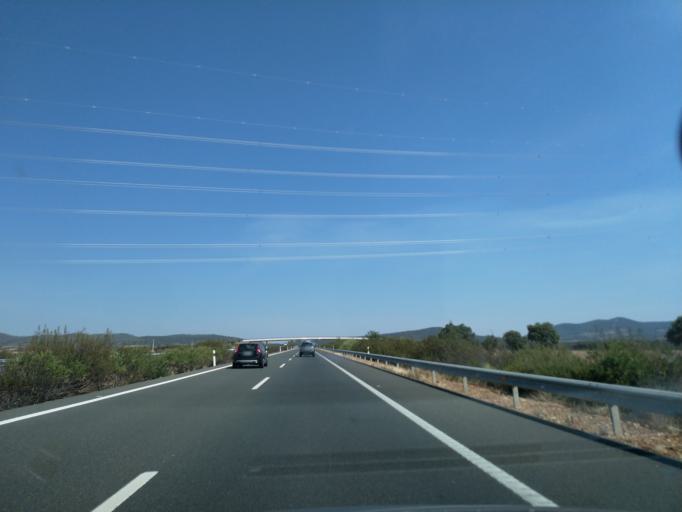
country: ES
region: Extremadura
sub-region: Provincia de Badajoz
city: Carmonita
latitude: 39.1264
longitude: -6.2769
